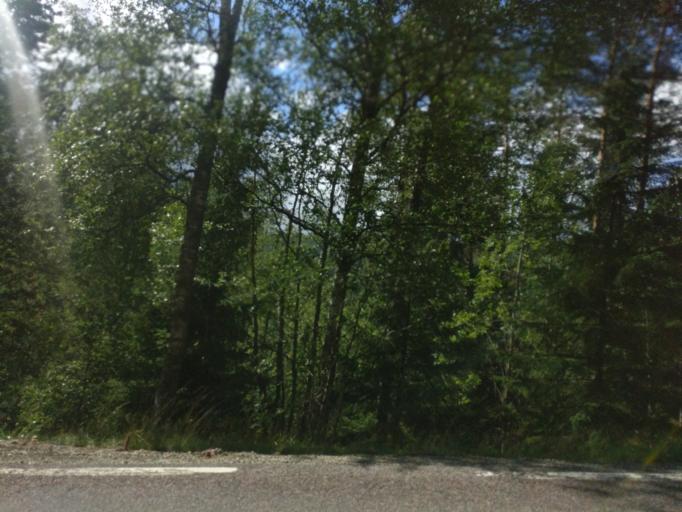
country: SE
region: Vaermland
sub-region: Hagfors Kommun
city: Ekshaerad
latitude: 60.3413
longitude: 13.3518
